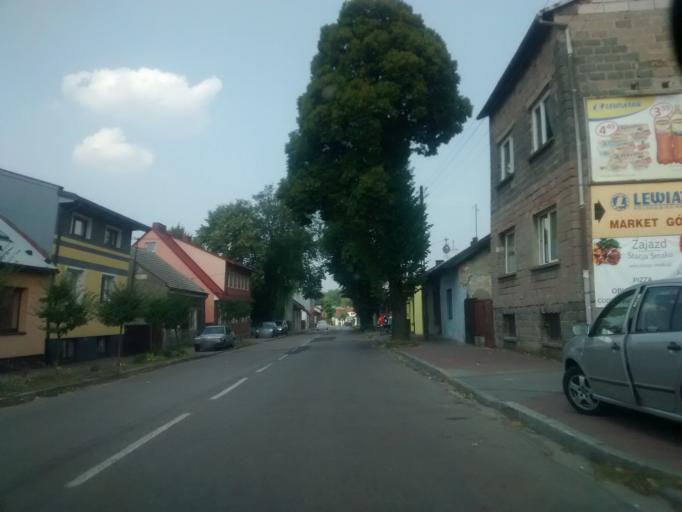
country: PL
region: Silesian Voivodeship
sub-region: Powiat czestochowski
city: Potok Zloty
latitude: 50.7199
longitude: 19.4361
